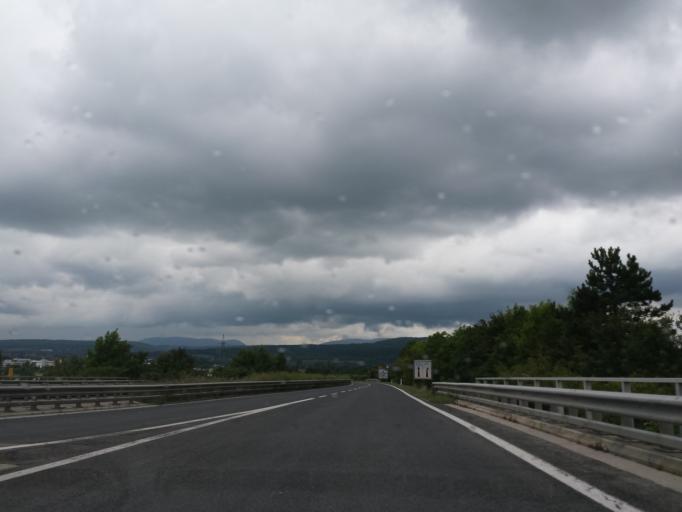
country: AT
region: Lower Austria
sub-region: Politischer Bezirk Baden
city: Leobersdorf
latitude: 47.9349
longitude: 16.2083
